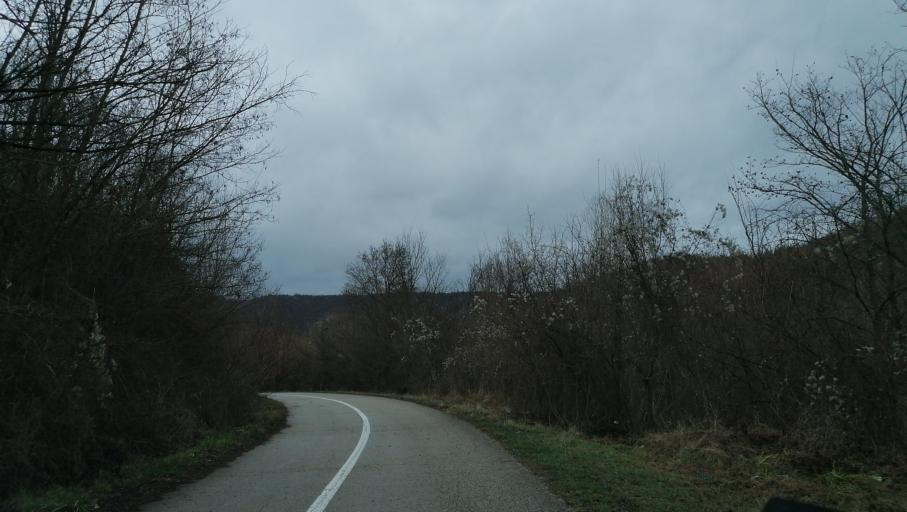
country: RS
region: Central Serbia
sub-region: Pirotski Okrug
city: Dimitrovgrad
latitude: 42.9266
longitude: 22.7692
